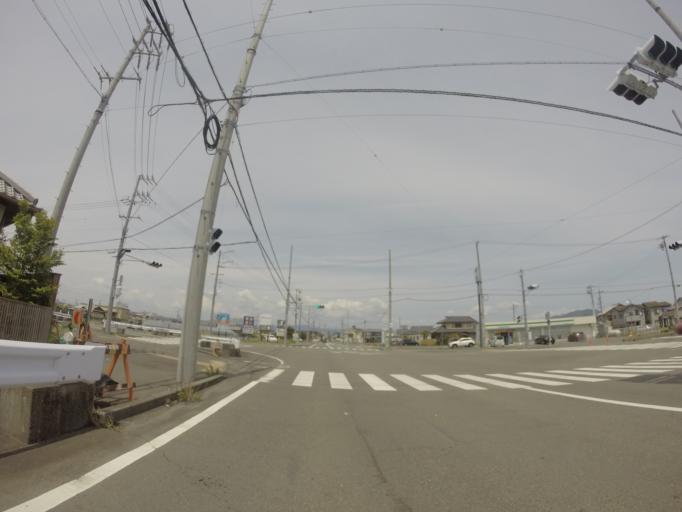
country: JP
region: Shizuoka
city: Fujieda
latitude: 34.8424
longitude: 138.2933
